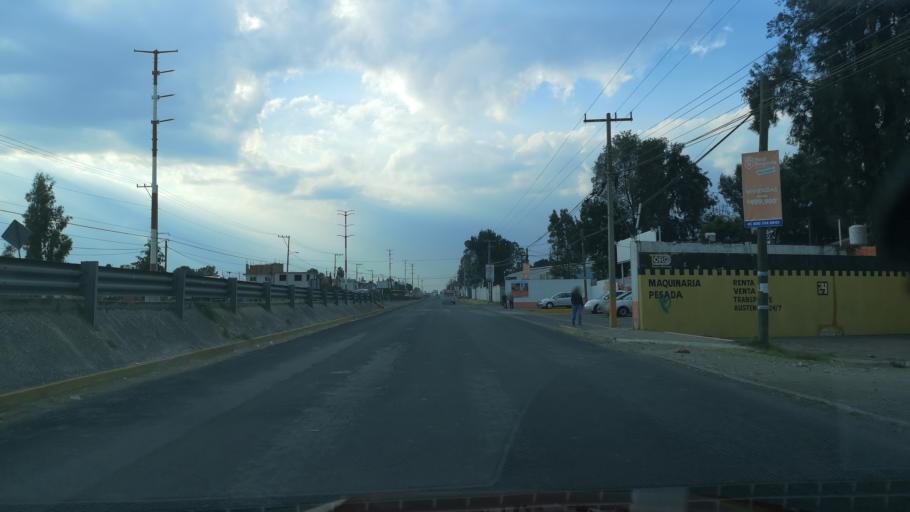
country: MX
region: Puebla
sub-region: Juan C. Bonilla
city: Santa Maria Zacatepec
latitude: 19.1092
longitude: -98.3529
